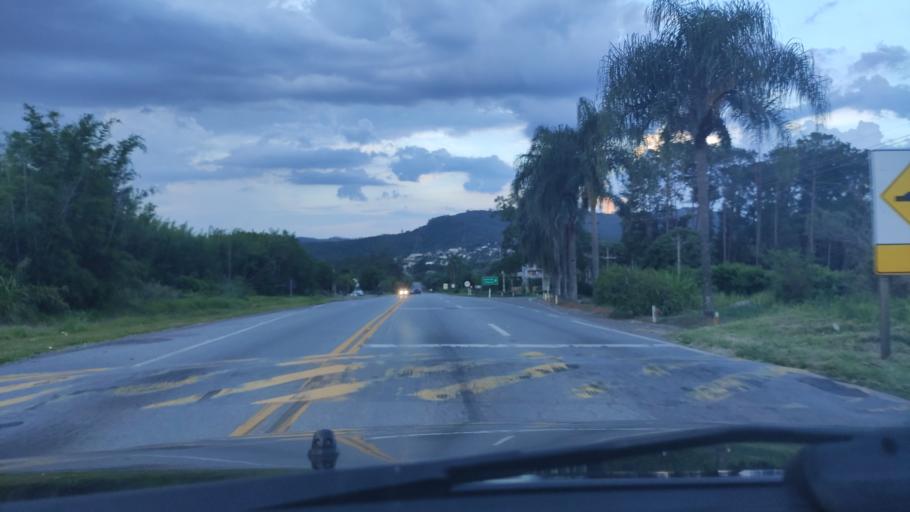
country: BR
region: Sao Paulo
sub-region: Braganca Paulista
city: Braganca Paulista
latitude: -22.8819
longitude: -46.5371
